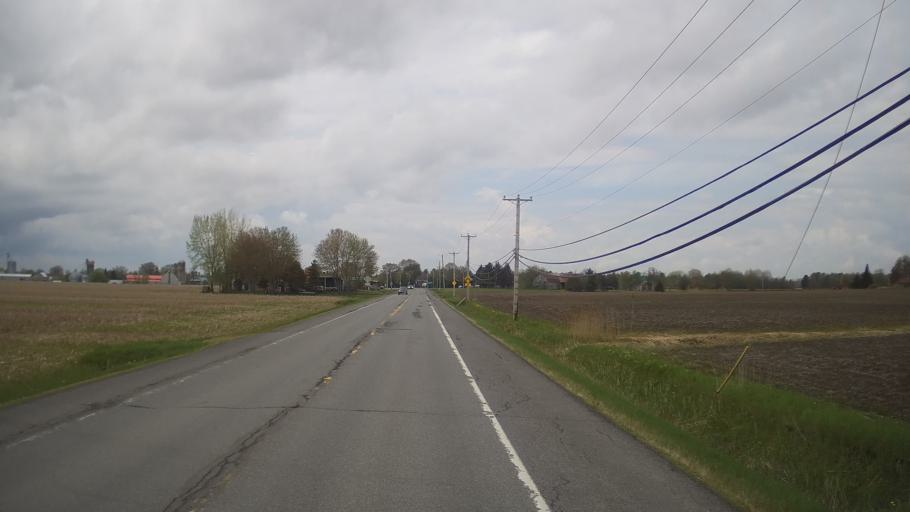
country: CA
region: Quebec
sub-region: Monteregie
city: Saint-Jean-sur-Richelieu
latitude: 45.3263
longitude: -73.1807
